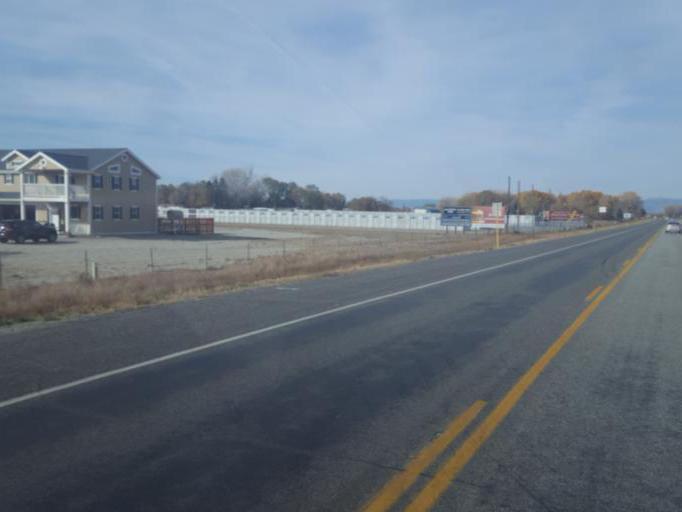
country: US
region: Colorado
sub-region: Alamosa County
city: Alamosa East
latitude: 37.4734
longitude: -105.8153
